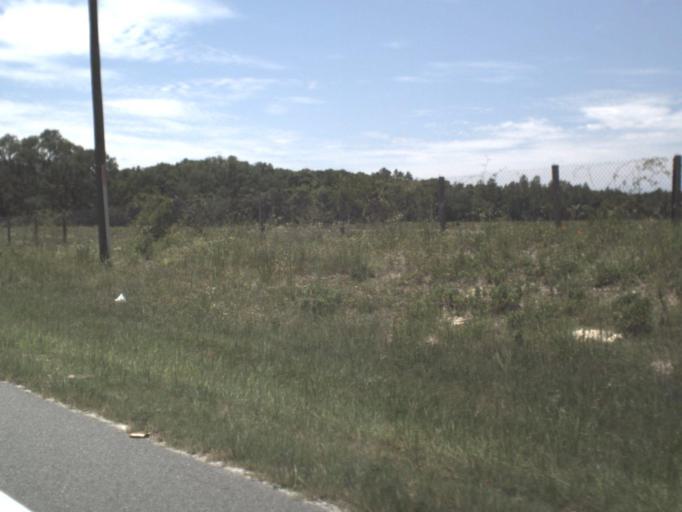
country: US
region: Florida
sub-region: Dixie County
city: Cross City
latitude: 29.7544
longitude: -82.9836
